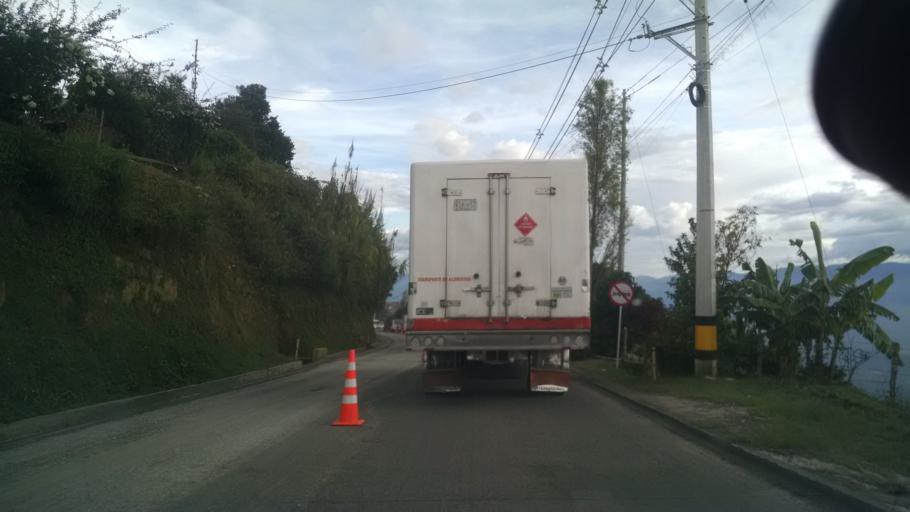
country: CO
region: Antioquia
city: Santa Barbara
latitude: 5.8908
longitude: -75.5718
